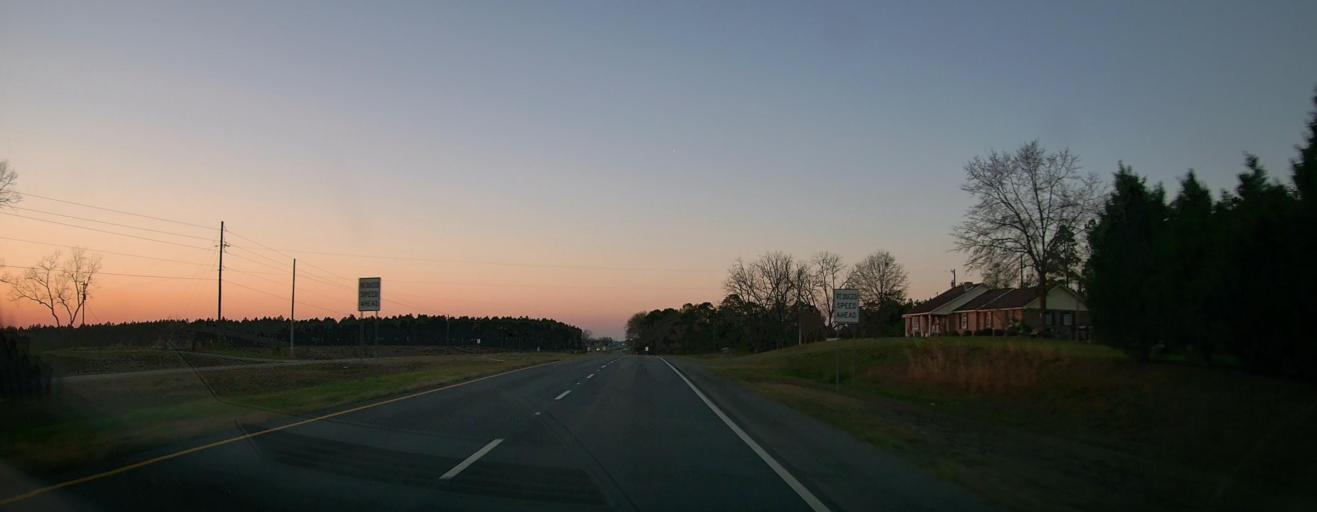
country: US
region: Georgia
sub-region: Dodge County
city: Eastman
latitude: 32.1578
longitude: -83.1466
